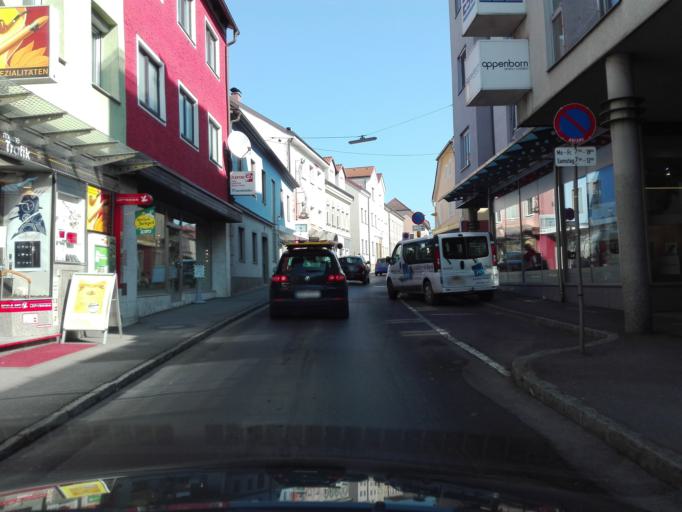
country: AT
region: Upper Austria
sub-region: Politischer Bezirk Urfahr-Umgebung
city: Gallneukirchen
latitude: 48.3540
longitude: 14.4169
